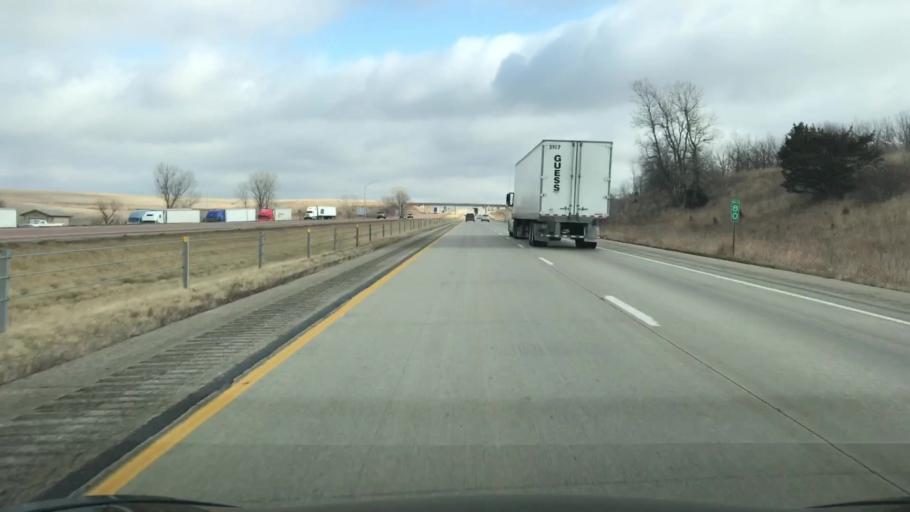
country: US
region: Iowa
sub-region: Guthrie County
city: Guthrie Center
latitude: 41.4967
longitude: -94.5734
